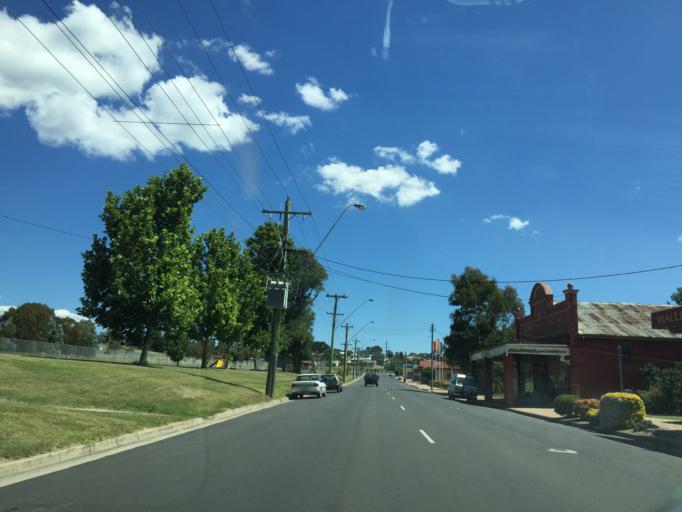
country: AU
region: New South Wales
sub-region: Lithgow
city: Portland
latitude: -33.4082
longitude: 150.0671
